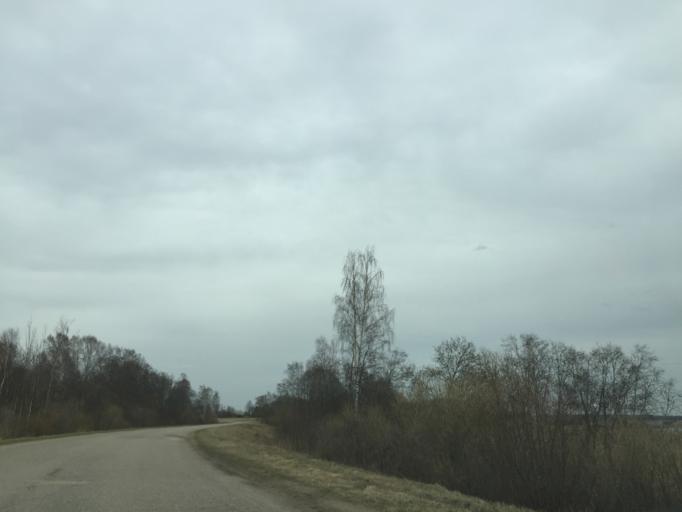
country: LV
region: Ilukste
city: Ilukste
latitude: 56.0465
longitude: 26.2799
